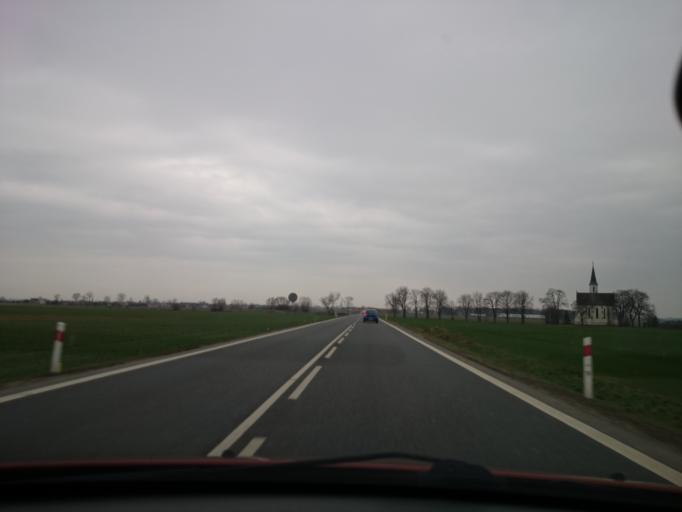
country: PL
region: Opole Voivodeship
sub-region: Powiat nyski
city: Sidzina
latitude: 50.5834
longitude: 17.4663
